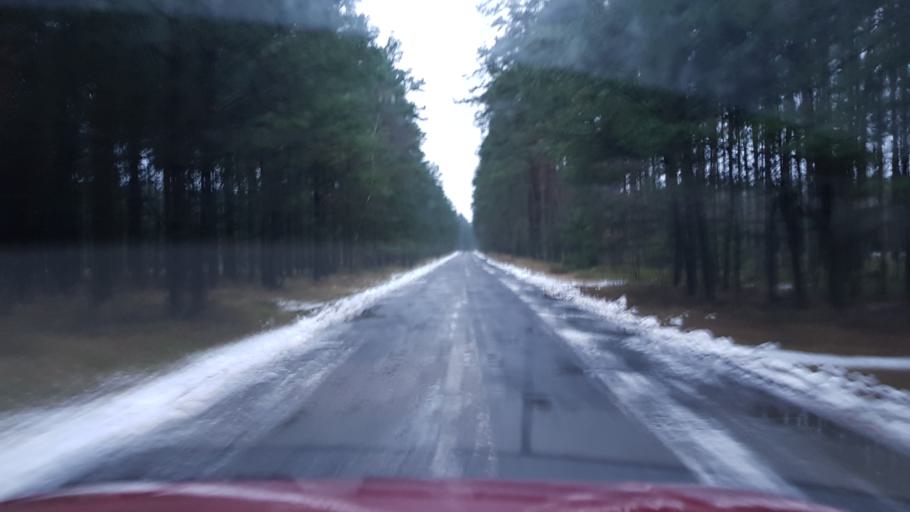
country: PL
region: West Pomeranian Voivodeship
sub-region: Powiat goleniowski
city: Goleniow
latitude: 53.4850
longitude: 14.8528
